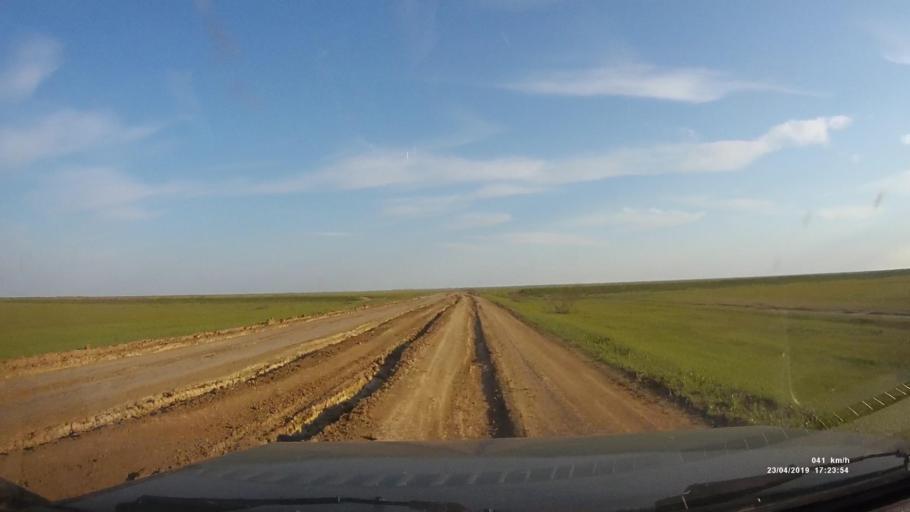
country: RU
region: Kalmykiya
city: Priyutnoye
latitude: 46.1596
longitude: 43.5081
